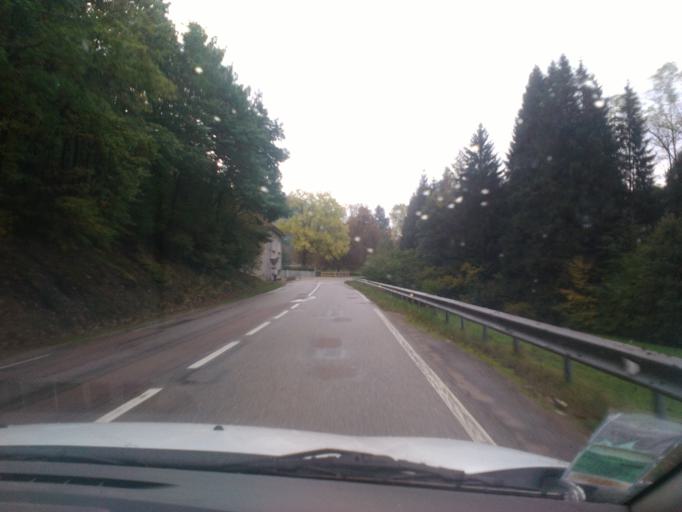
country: FR
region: Lorraine
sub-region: Departement des Vosges
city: Bruyeres
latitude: 48.2206
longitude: 6.7230
